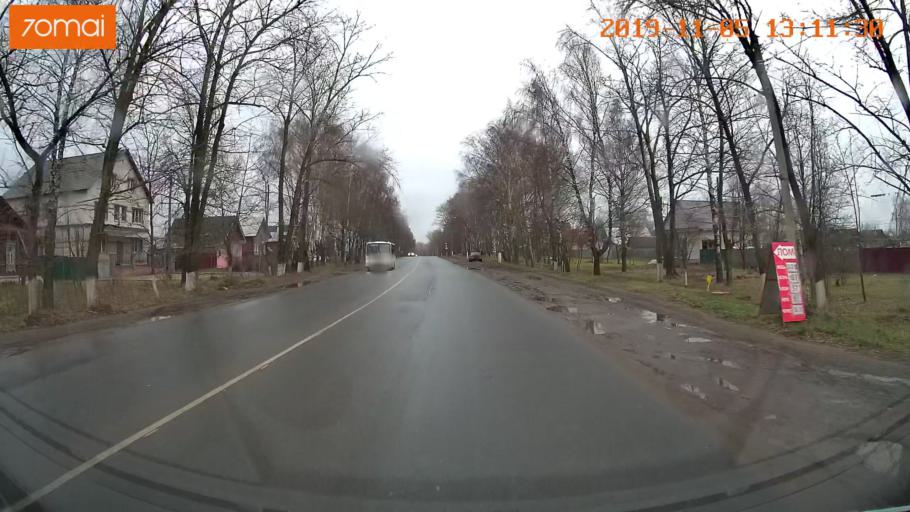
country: RU
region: Ivanovo
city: Shuya
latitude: 56.8588
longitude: 41.3401
